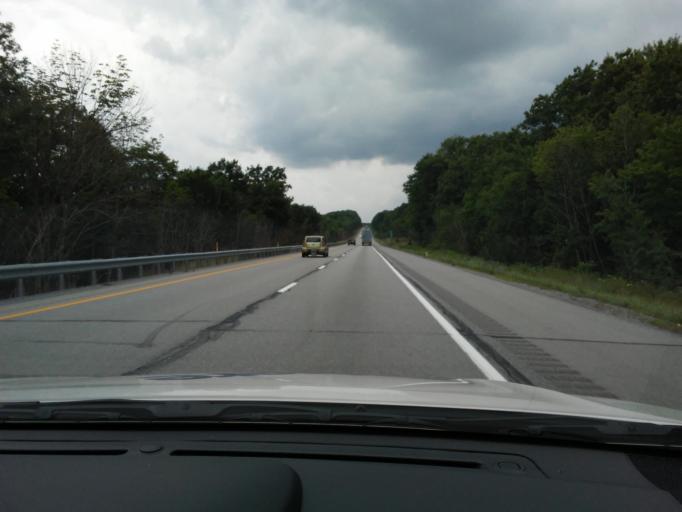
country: US
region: Pennsylvania
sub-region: Clearfield County
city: Troy
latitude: 40.9878
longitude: -78.1959
